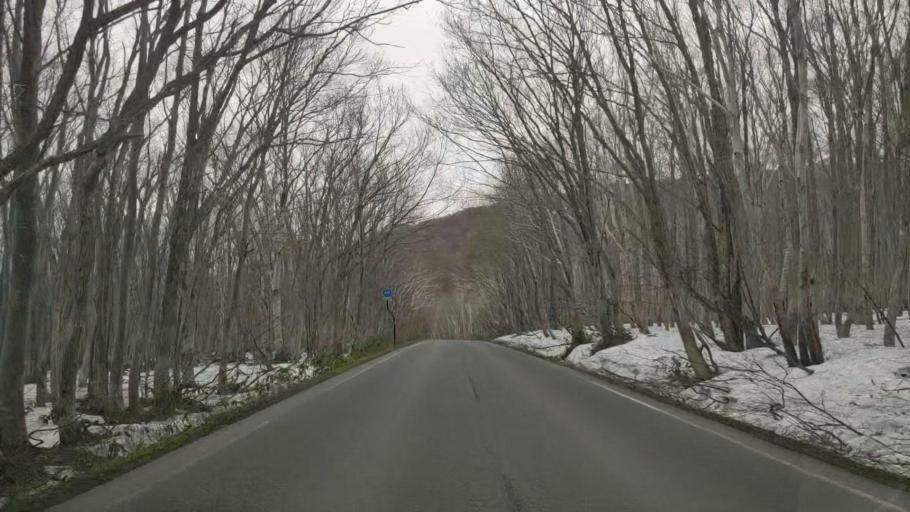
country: JP
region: Aomori
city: Aomori Shi
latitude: 40.6943
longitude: 140.9080
